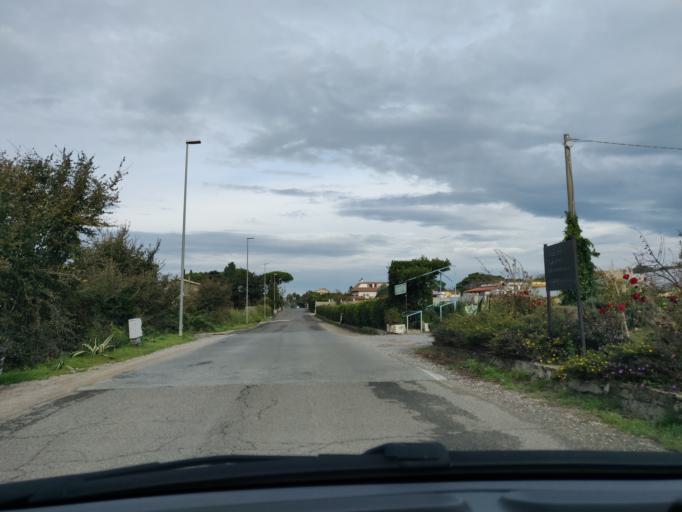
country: IT
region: Latium
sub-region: Citta metropolitana di Roma Capitale
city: Civitavecchia
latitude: 42.1019
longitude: 11.8128
